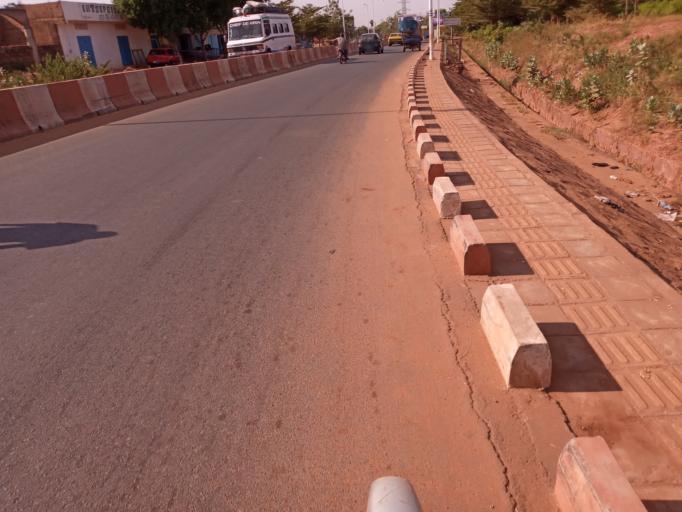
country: ML
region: Bamako
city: Bamako
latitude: 12.6349
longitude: -7.9235
